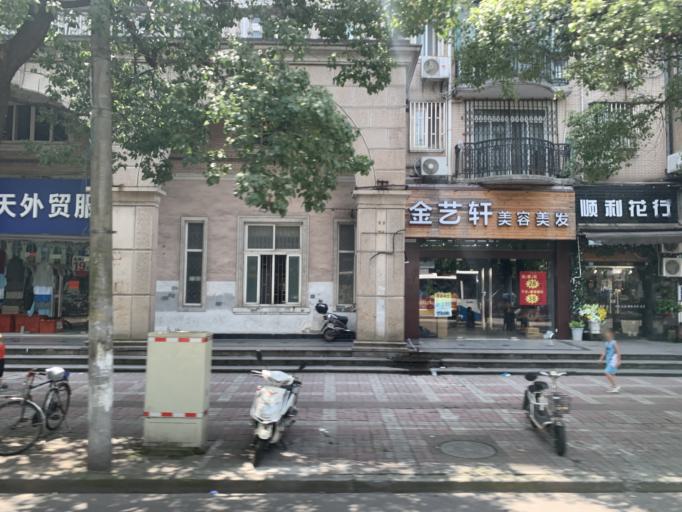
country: CN
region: Shanghai Shi
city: Pudong
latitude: 31.2473
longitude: 121.5499
